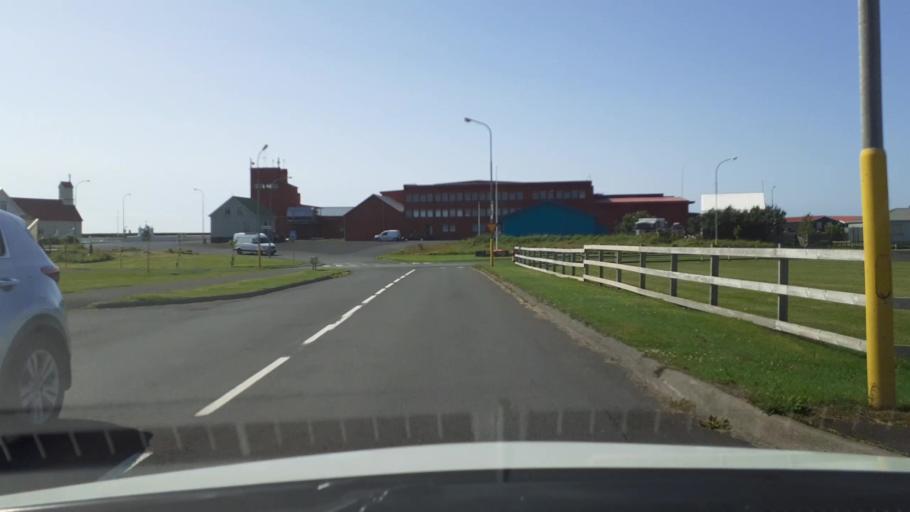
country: IS
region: South
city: Selfoss
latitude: 63.8372
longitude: -21.0621
